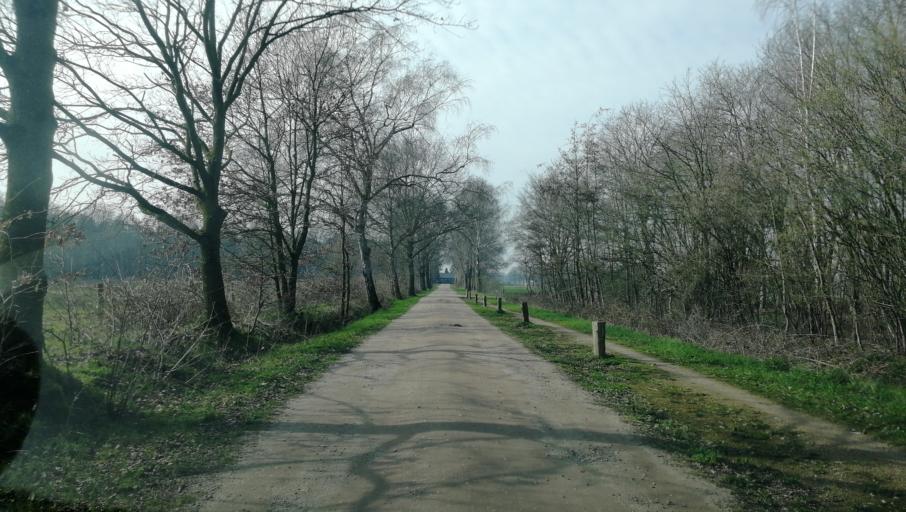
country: NL
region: Limburg
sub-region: Gemeente Peel en Maas
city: Maasbree
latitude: 51.4351
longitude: 6.0610
